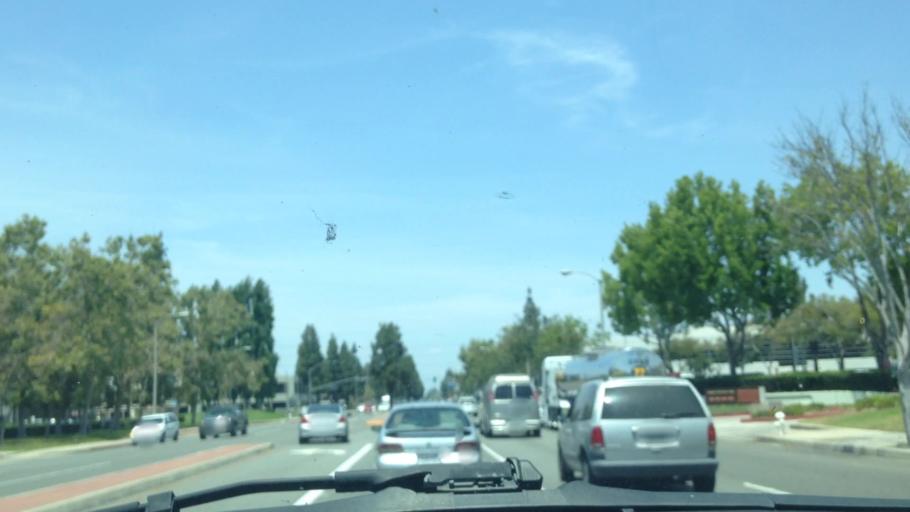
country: US
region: California
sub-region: Orange County
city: Fountain Valley
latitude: 33.6974
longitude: -117.9195
